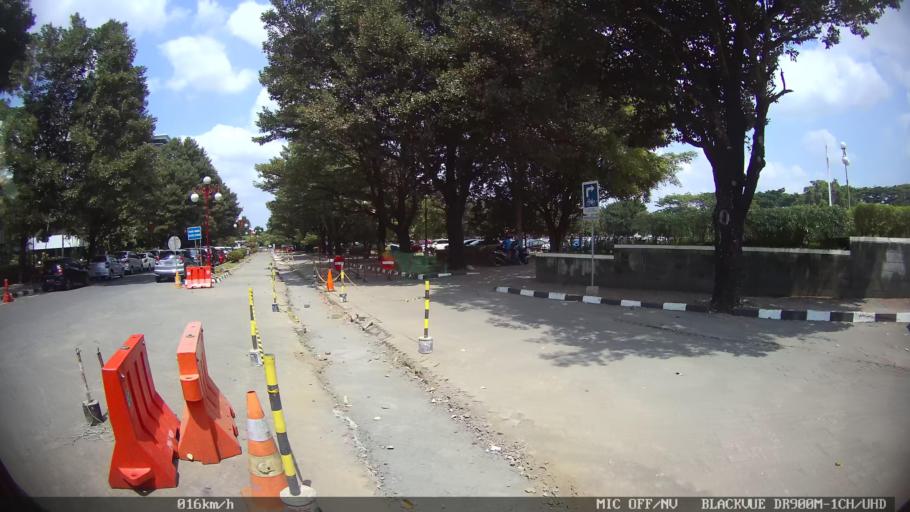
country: ID
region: Daerah Istimewa Yogyakarta
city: Yogyakarta
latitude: -7.7709
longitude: 110.3783
